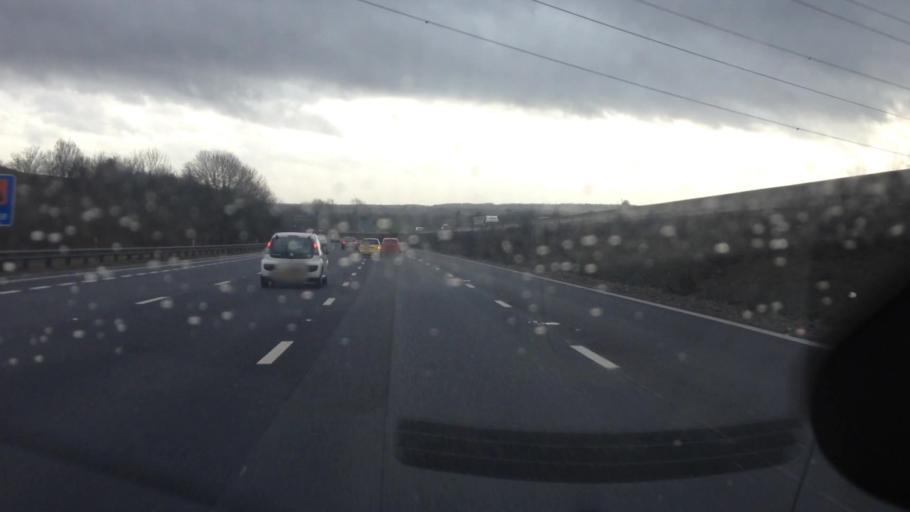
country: GB
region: England
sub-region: City and Borough of Wakefield
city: Horbury
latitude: 53.6754
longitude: -1.5520
